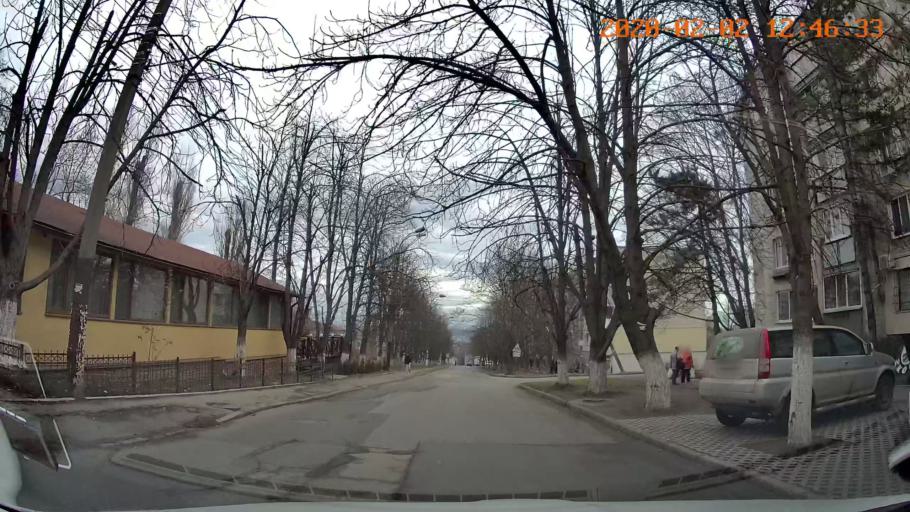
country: MD
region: Chisinau
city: Chisinau
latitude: 47.0094
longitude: 28.8189
